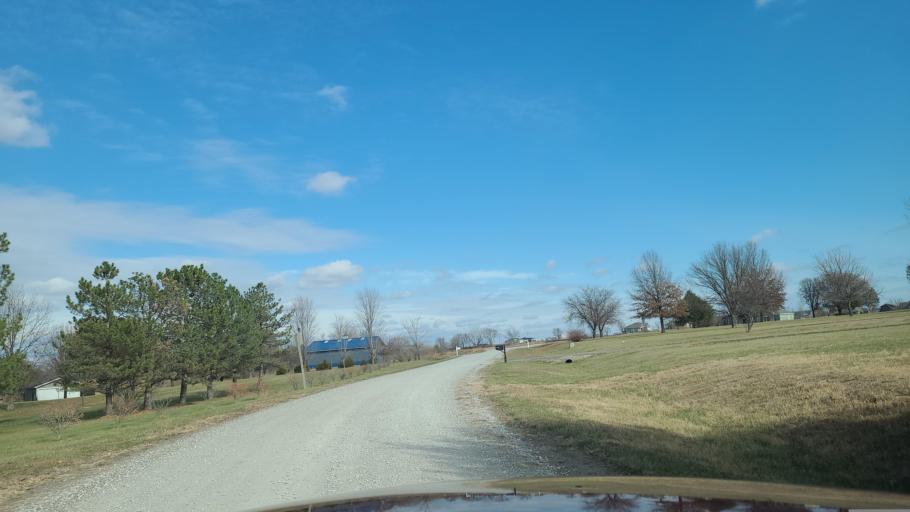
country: US
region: Kansas
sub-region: Douglas County
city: Eudora
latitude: 38.9160
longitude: -95.1079
